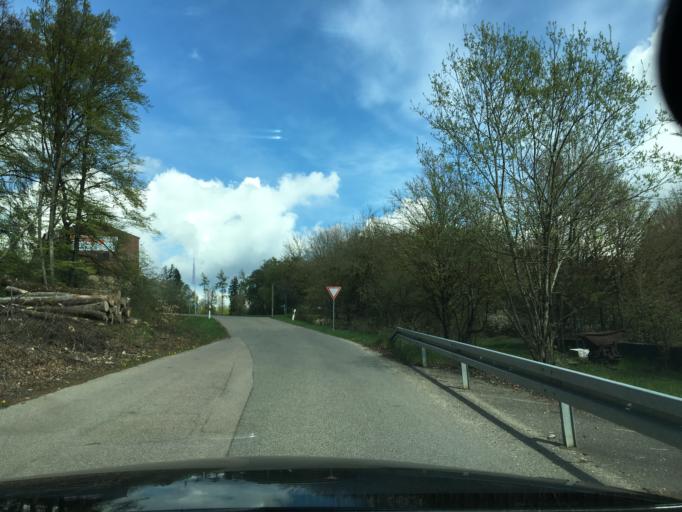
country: DE
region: Bavaria
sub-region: Regierungsbezirk Mittelfranken
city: Solnhofen
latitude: 48.8775
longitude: 10.9928
